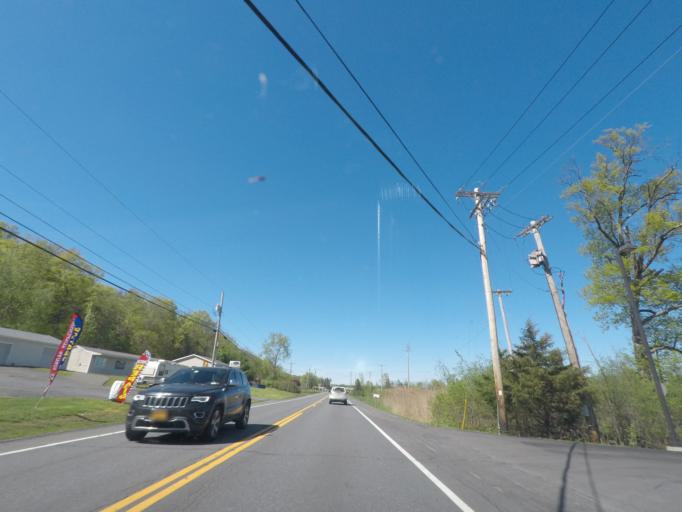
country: US
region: New York
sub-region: Greene County
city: Jefferson Heights
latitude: 42.2719
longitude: -73.8582
